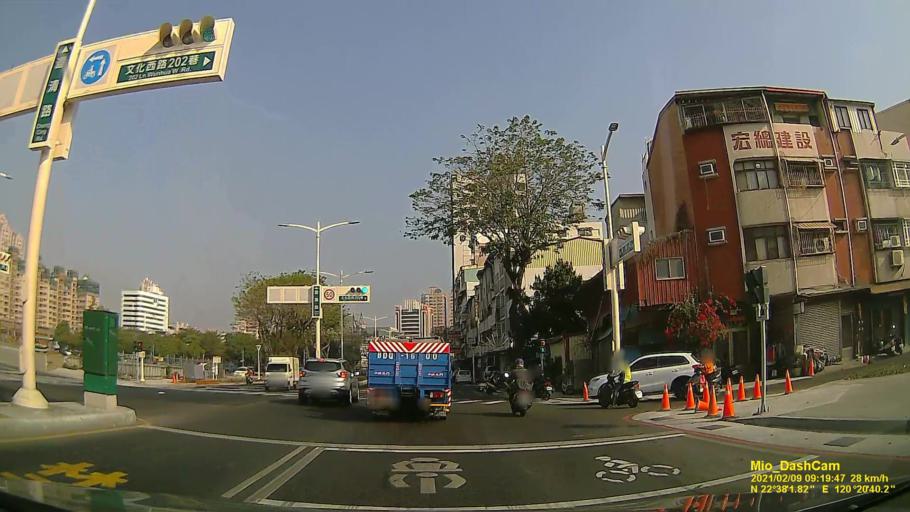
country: TW
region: Taiwan
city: Fengshan
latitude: 22.6338
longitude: 120.3445
